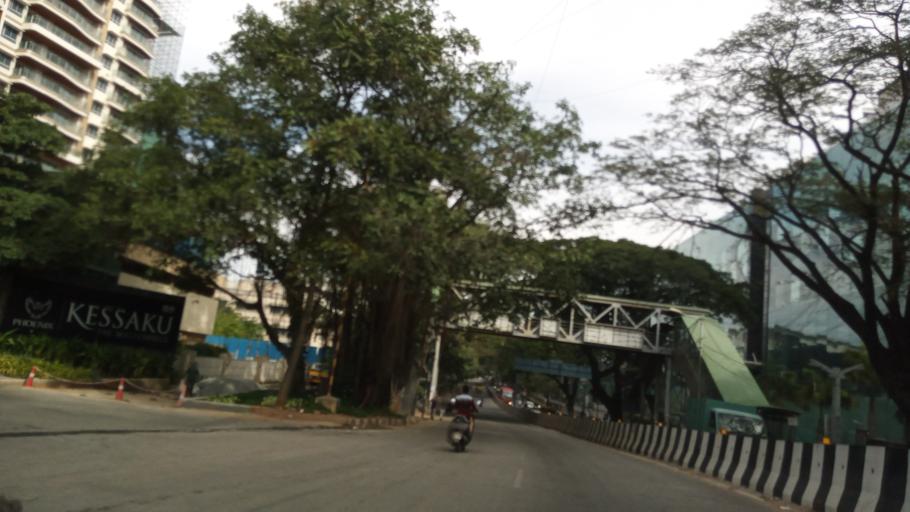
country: IN
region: Karnataka
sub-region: Bangalore Urban
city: Bangalore
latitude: 13.0096
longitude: 77.5544
